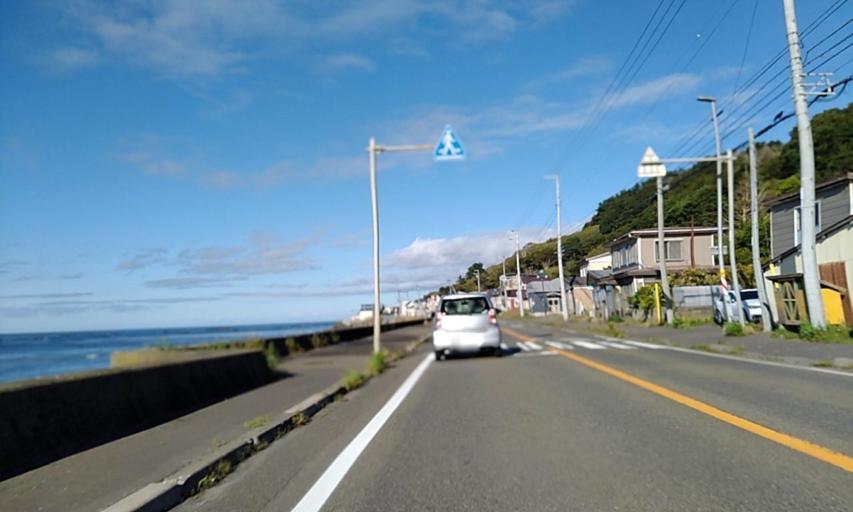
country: JP
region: Hokkaido
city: Shizunai-furukawacho
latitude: 42.1770
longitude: 142.7425
